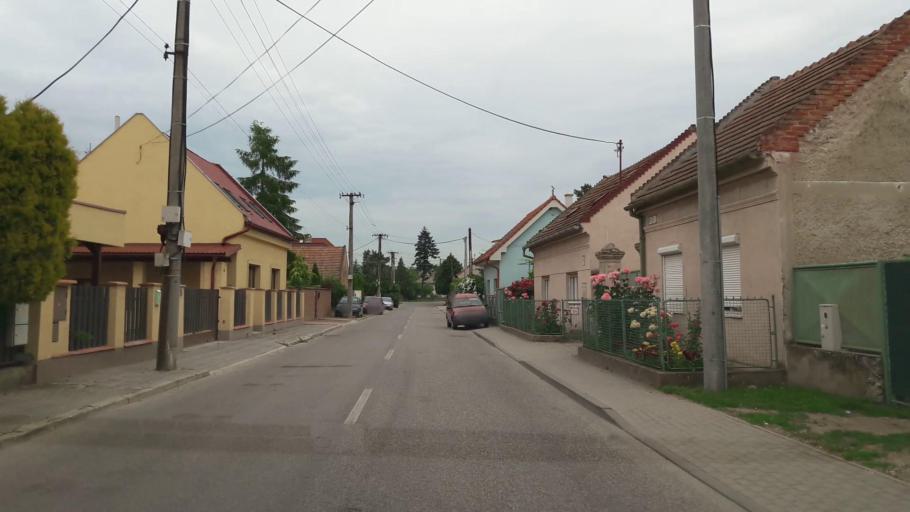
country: SK
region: Bratislavsky
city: Senec
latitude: 48.2118
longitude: 17.3601
